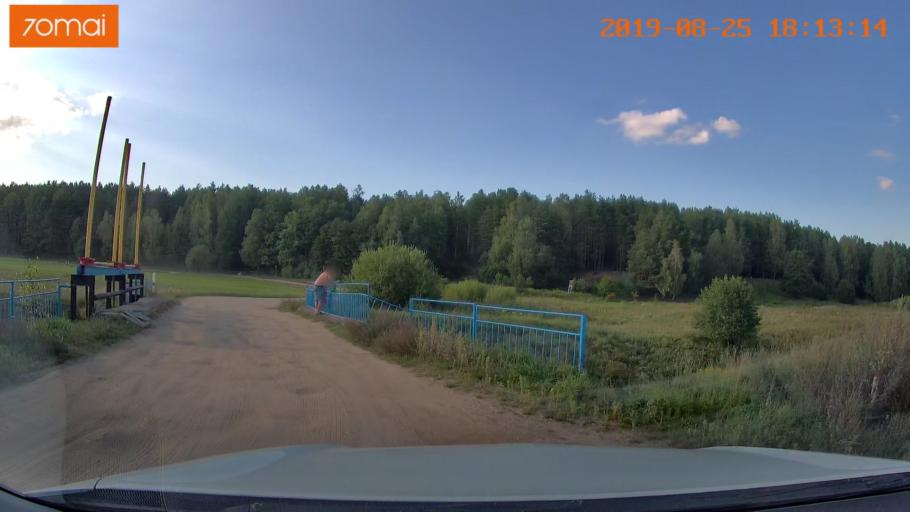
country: BY
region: Minsk
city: Khatsyezhyna
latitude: 53.9434
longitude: 27.3070
